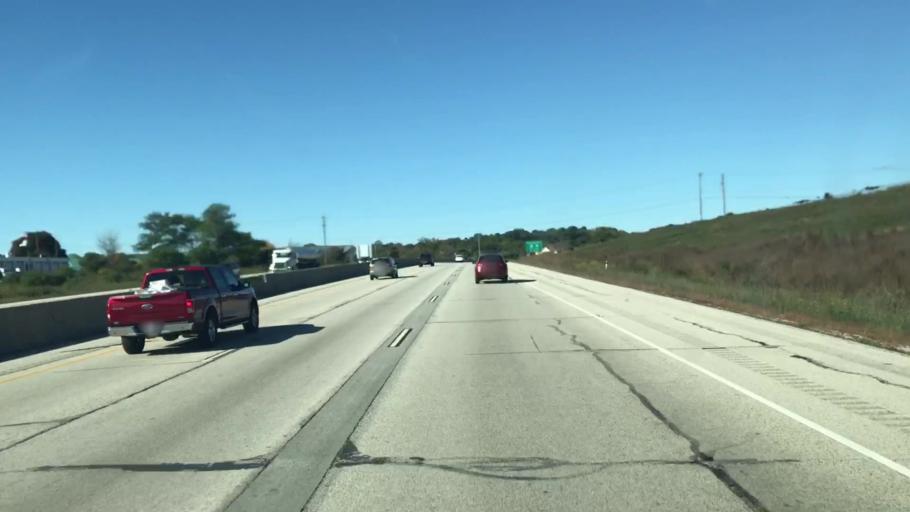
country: US
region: Wisconsin
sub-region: Waukesha County
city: Pewaukee
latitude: 43.0461
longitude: -88.2630
